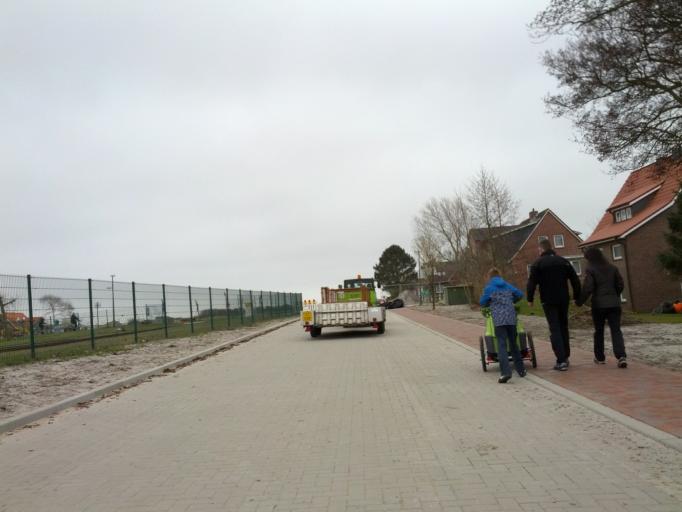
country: DE
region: Lower Saxony
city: Langeoog
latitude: 53.7445
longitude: 7.4872
